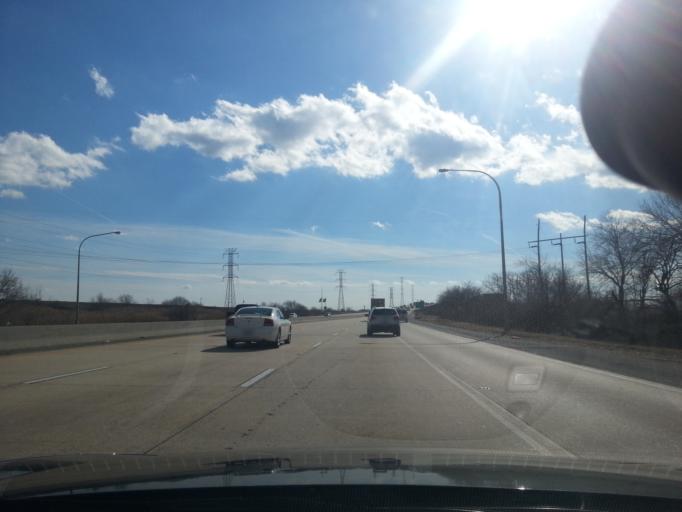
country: US
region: Delaware
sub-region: New Castle County
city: Wilmington
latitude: 39.7334
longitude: -75.5239
